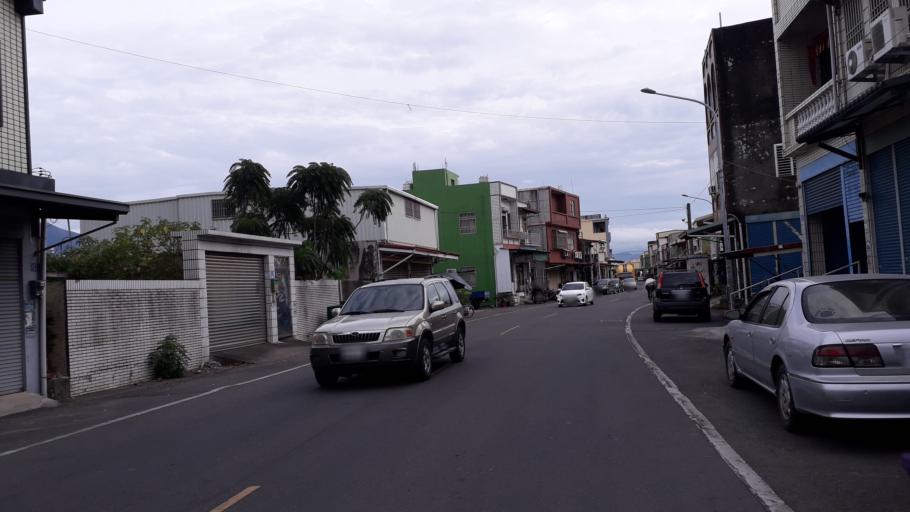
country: TW
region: Taiwan
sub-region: Pingtung
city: Pingtung
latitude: 22.3602
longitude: 120.5972
